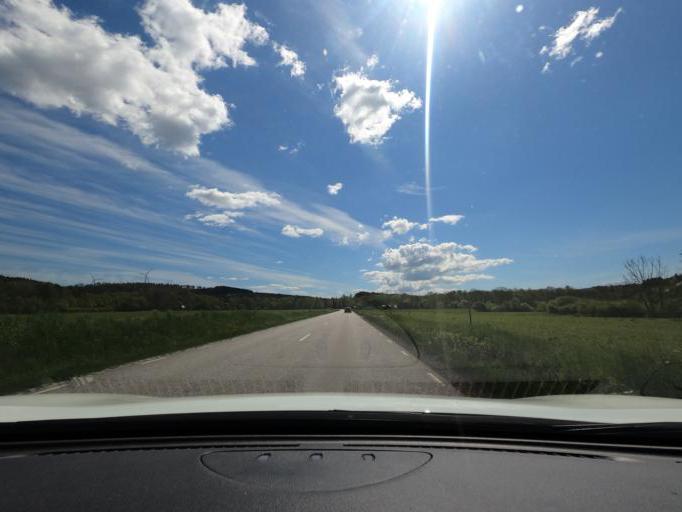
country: SE
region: Halland
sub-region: Kungsbacka Kommun
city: Fjaeras kyrkby
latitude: 57.4205
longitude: 12.2029
